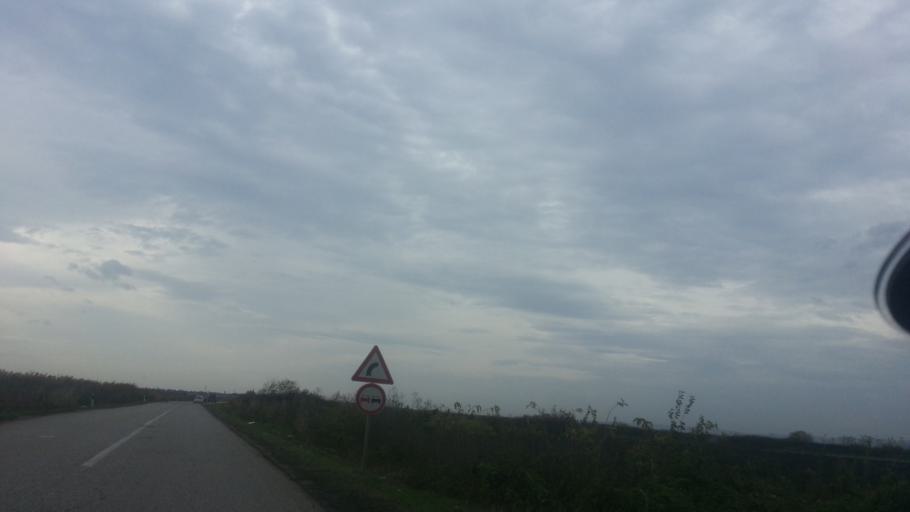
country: RS
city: Putinci
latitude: 44.9892
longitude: 20.0076
